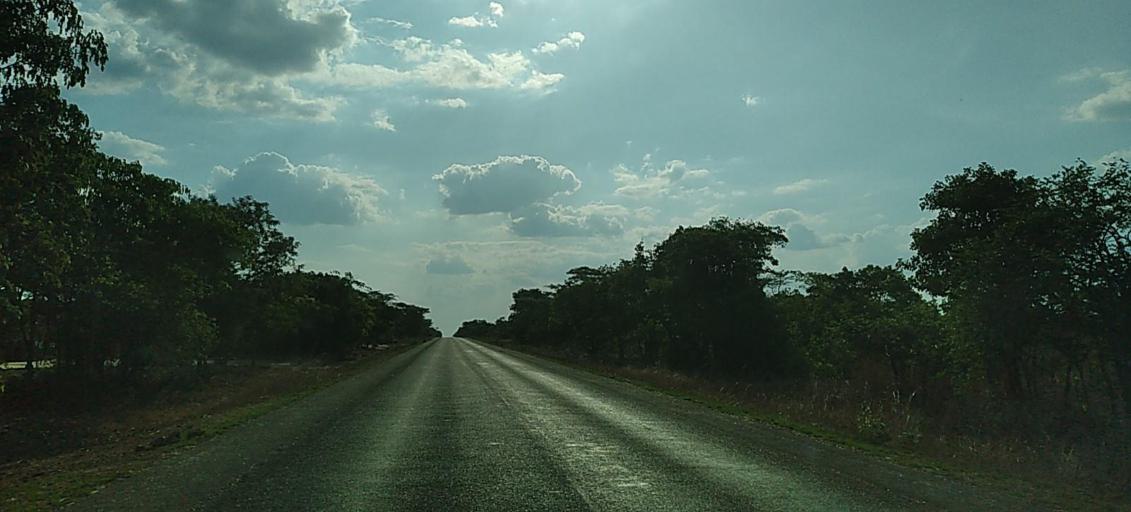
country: ZM
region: Copperbelt
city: Mpongwe
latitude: -13.3893
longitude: 28.3789
